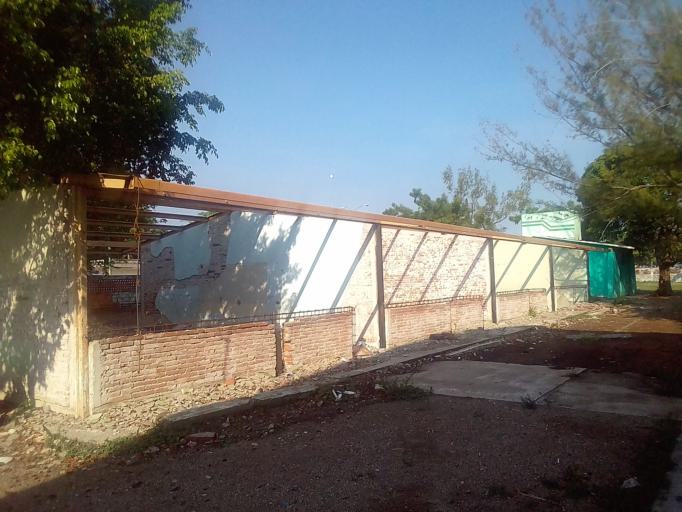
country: MX
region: Oaxaca
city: San Francisco Ixhuatan
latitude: 16.3398
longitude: -94.5137
